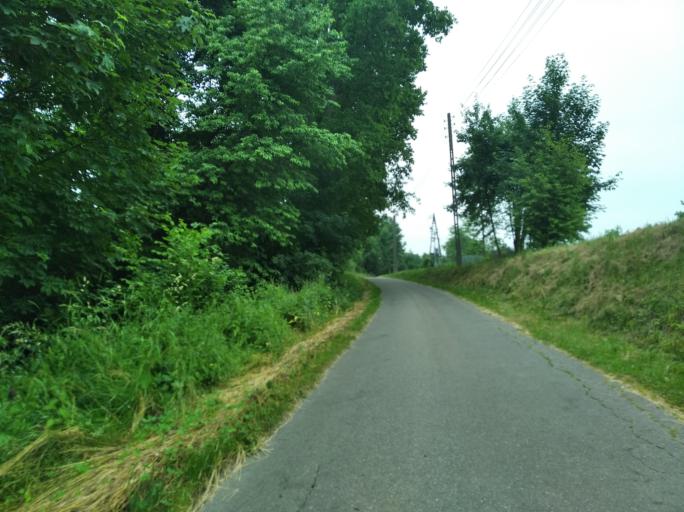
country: PL
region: Subcarpathian Voivodeship
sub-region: Powiat brzozowski
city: Jablonica Polska
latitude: 49.6931
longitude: 21.8896
